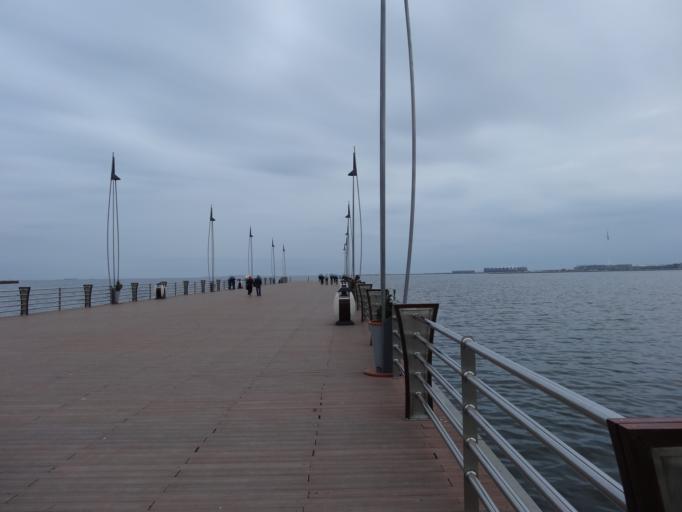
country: AZ
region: Baki
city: Badamdar
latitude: 40.3678
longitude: 49.8438
